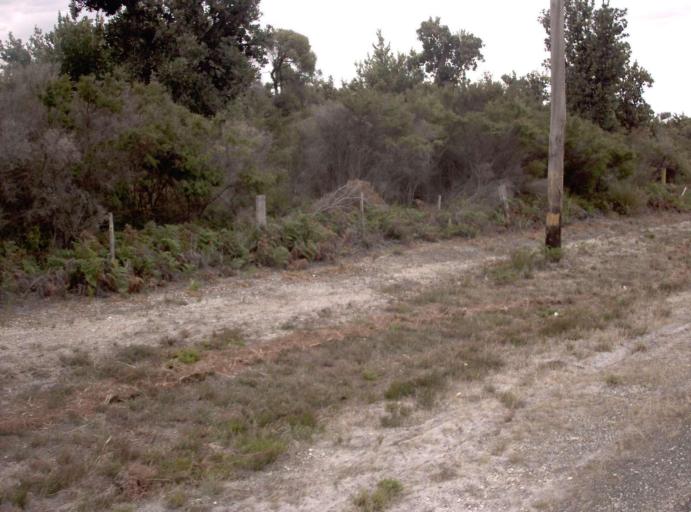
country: AU
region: Victoria
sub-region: Wellington
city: Sale
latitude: -38.1693
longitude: 147.3855
